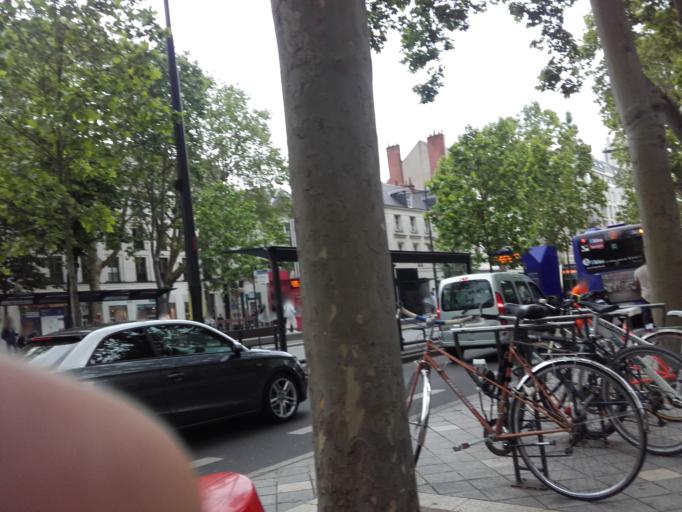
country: FR
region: Centre
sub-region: Departement d'Indre-et-Loire
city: Tours
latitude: 47.3891
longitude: 0.6891
